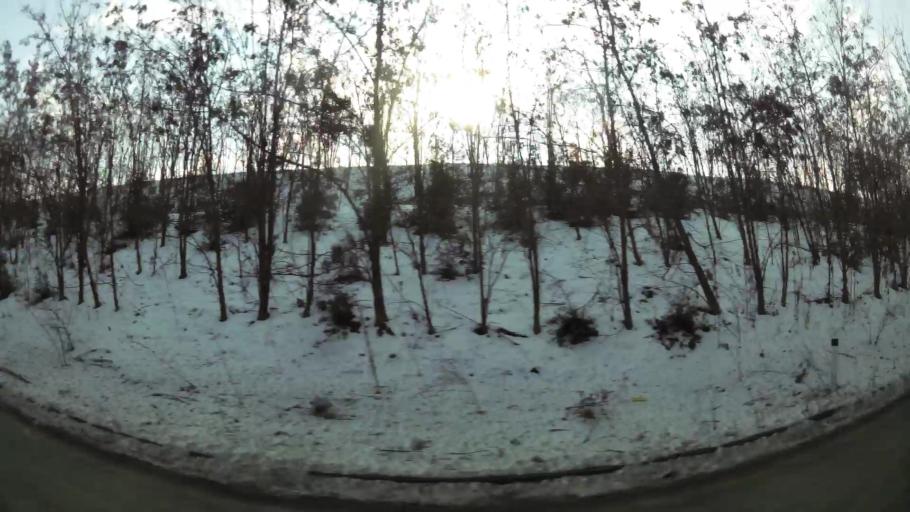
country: MK
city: Creshevo
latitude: 42.0337
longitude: 21.5230
